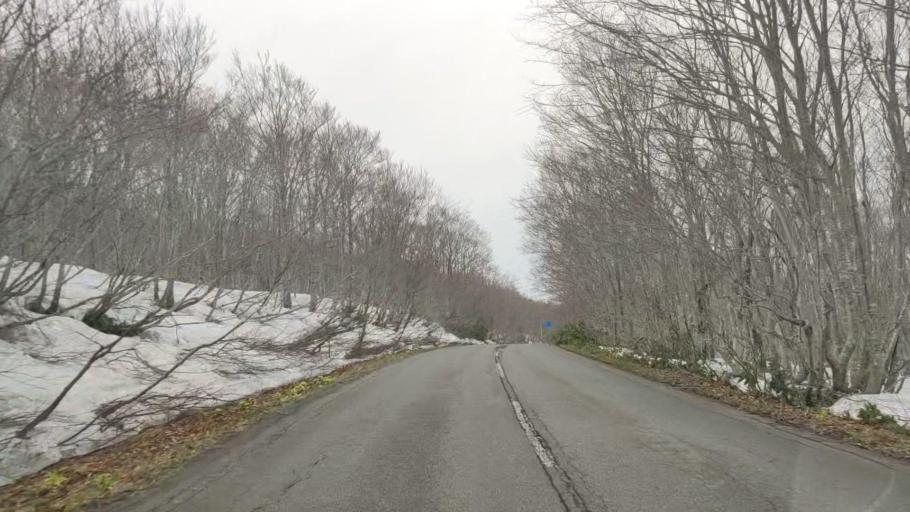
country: JP
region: Aomori
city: Aomori Shi
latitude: 40.6477
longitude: 140.9446
